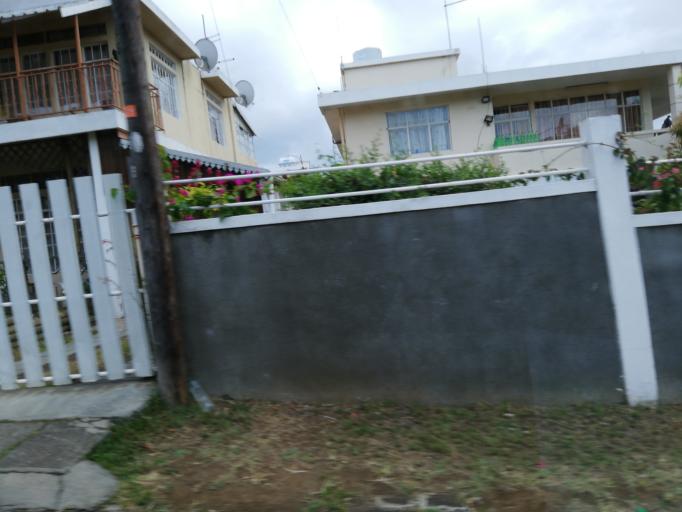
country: MU
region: Black River
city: Gros Cailloux
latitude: -20.2325
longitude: 57.4540
